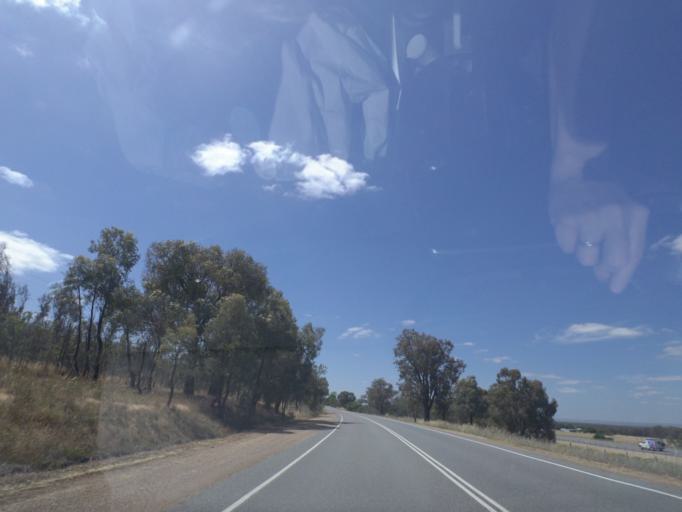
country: AU
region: Victoria
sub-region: Wangaratta
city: Wangaratta
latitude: -36.4574
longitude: 146.2363
